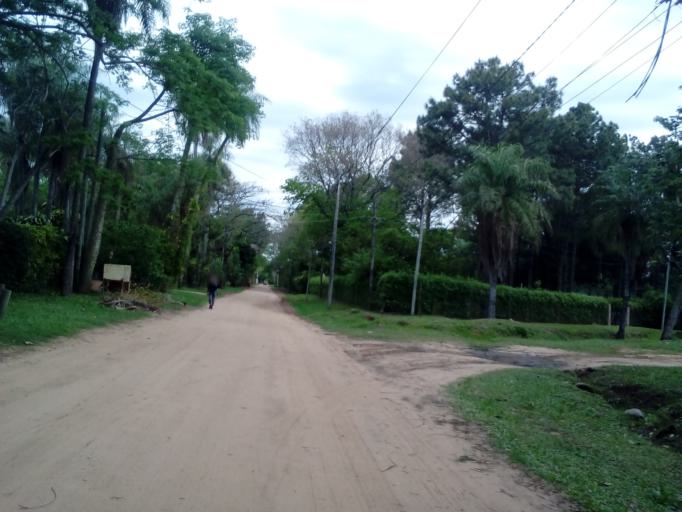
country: AR
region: Corrientes
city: San Luis del Palmar
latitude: -27.4604
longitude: -58.6610
